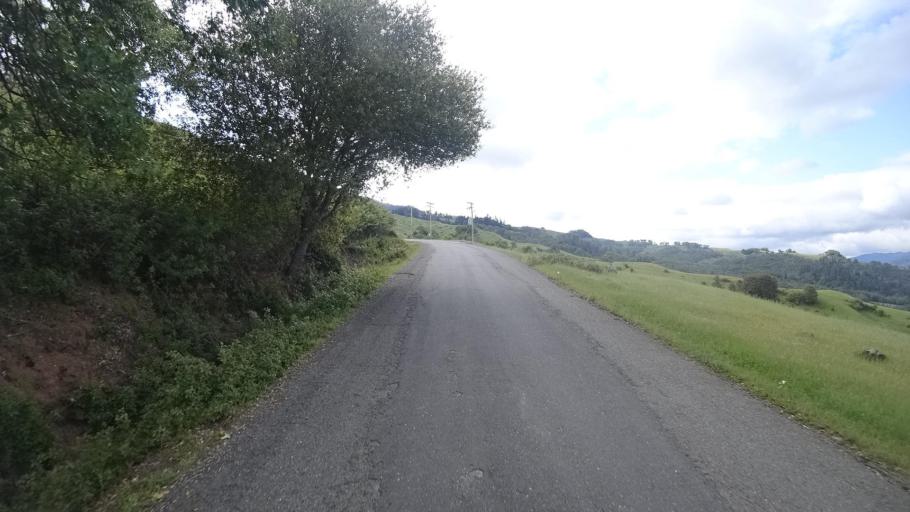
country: US
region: California
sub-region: Humboldt County
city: Redway
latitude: 40.1840
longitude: -123.5769
